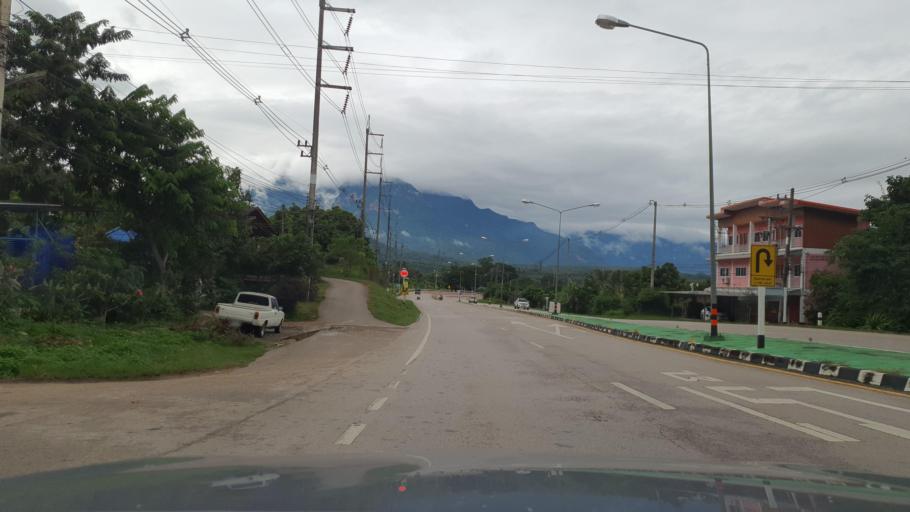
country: TH
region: Chiang Mai
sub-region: Amphoe Chiang Dao
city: Chiang Dao
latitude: 19.3212
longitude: 98.9547
